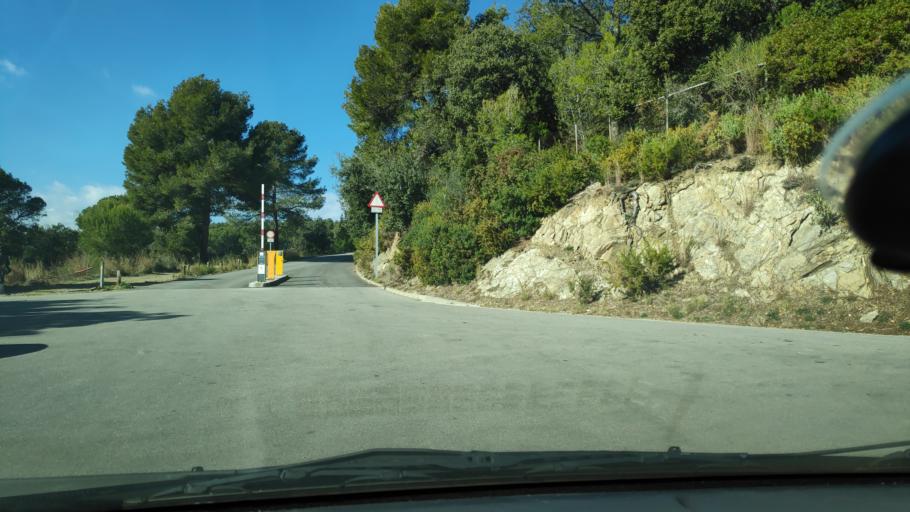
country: ES
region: Catalonia
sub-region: Provincia de Barcelona
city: Matadepera
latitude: 41.5979
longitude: 2.0105
